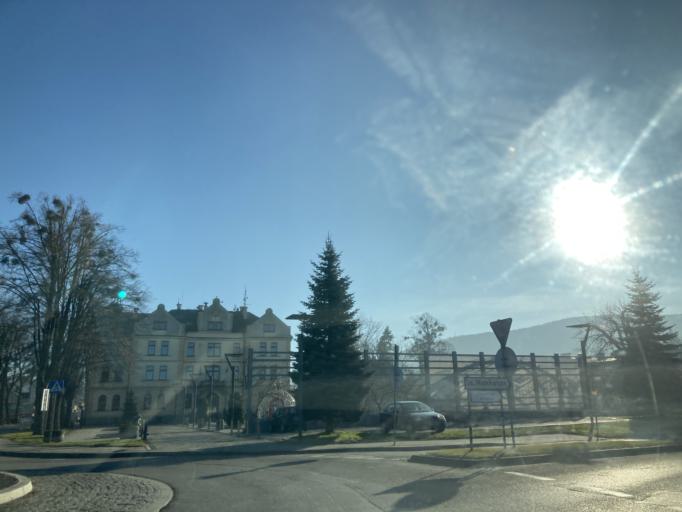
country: PL
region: Silesian Voivodeship
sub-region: Powiat cieszynski
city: Ustron
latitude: 49.7197
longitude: 18.8118
